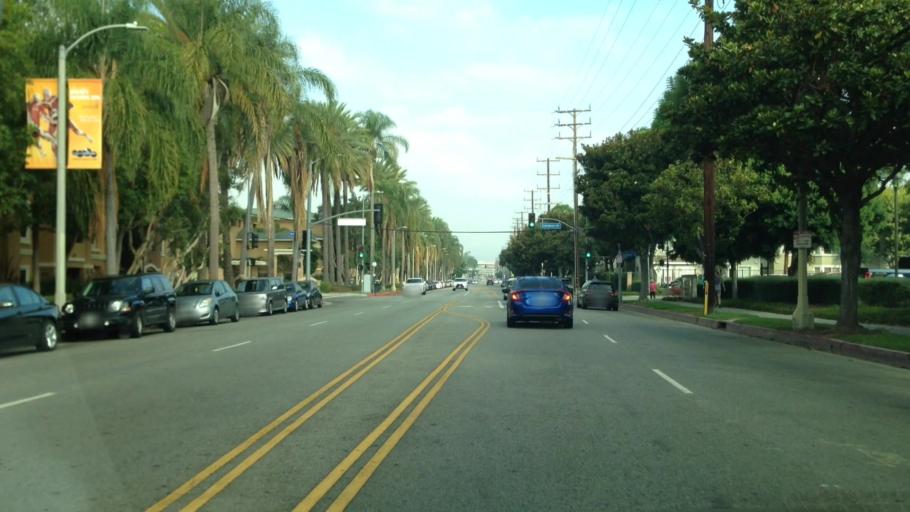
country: US
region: California
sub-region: Los Angeles County
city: Culver City
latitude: 34.0231
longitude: -118.4289
